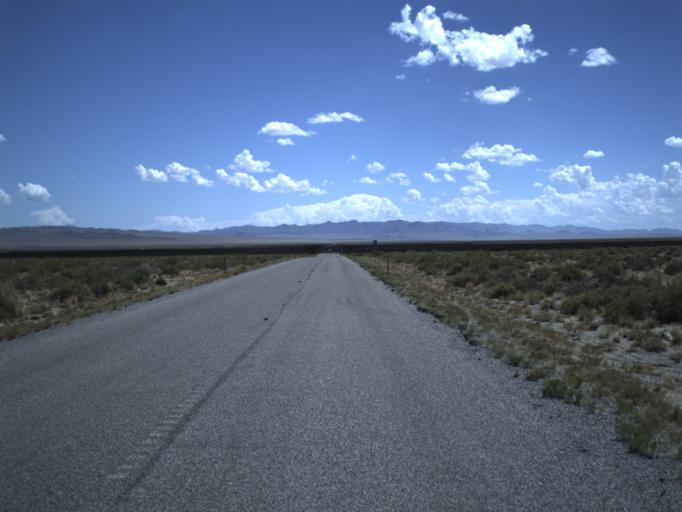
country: US
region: Nevada
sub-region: White Pine County
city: McGill
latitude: 39.0545
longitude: -114.0140
